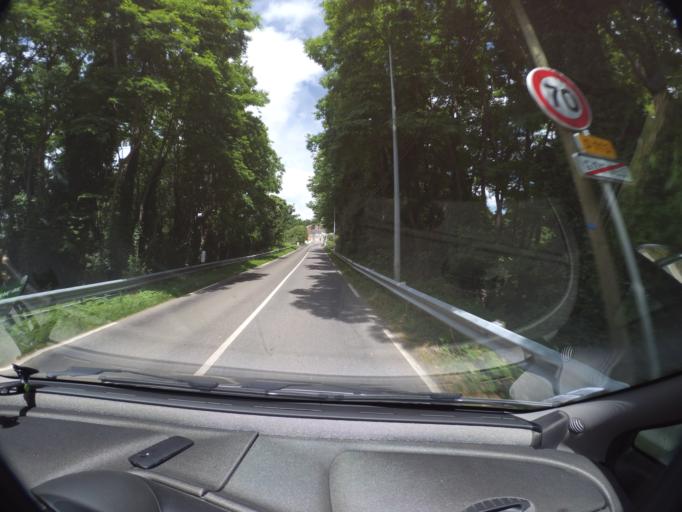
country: FR
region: Pays de la Loire
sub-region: Departement de la Loire-Atlantique
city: Gorges
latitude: 47.1060
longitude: -1.3047
